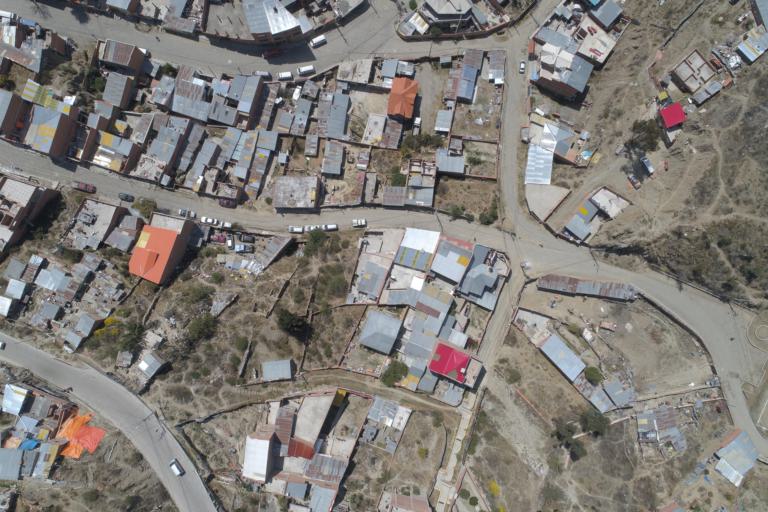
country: BO
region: La Paz
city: La Paz
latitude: -16.4988
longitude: -68.0986
